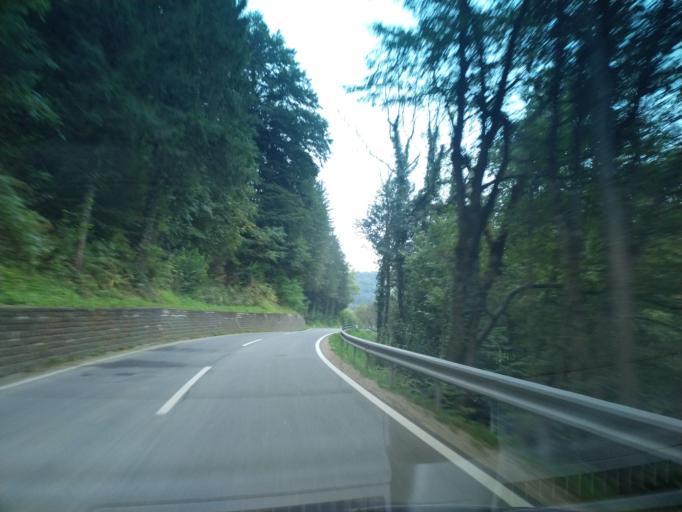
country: AT
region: Styria
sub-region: Politischer Bezirk Deutschlandsberg
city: Wernersdorf
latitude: 46.7174
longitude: 15.2185
